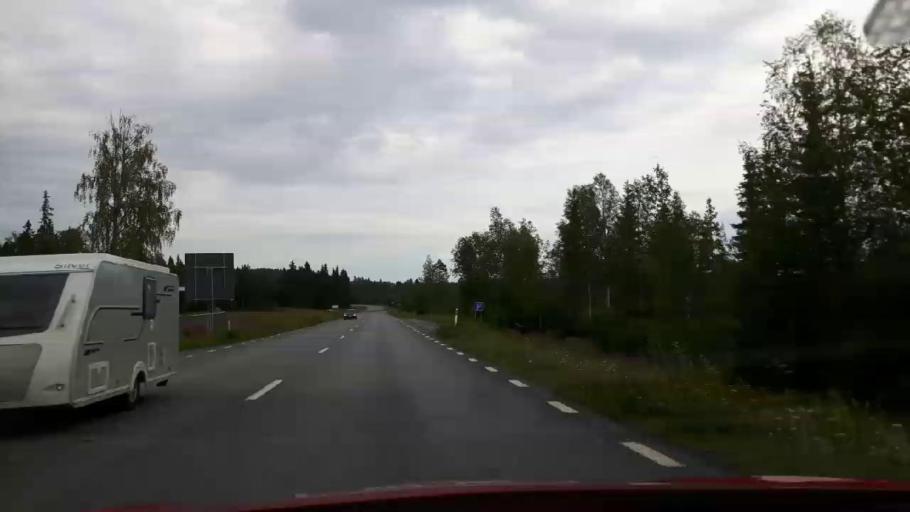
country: SE
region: Jaemtland
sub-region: Stroemsunds Kommun
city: Stroemsund
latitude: 63.5387
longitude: 15.3585
